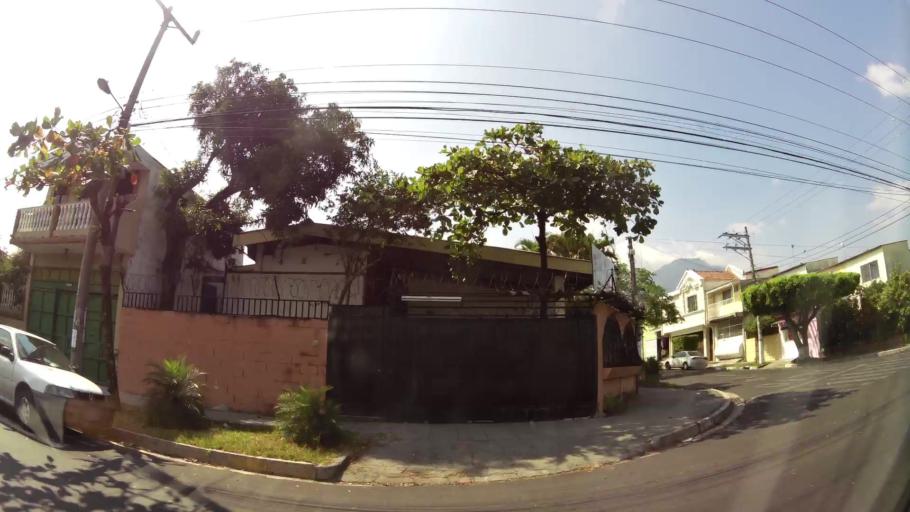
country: SV
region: San Salvador
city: Mejicanos
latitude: 13.7203
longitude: -89.2124
